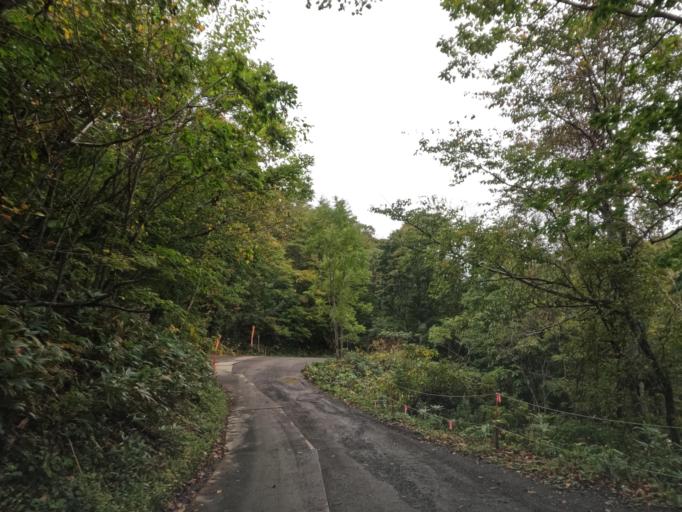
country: JP
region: Hokkaido
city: Date
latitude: 42.4976
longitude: 140.9284
